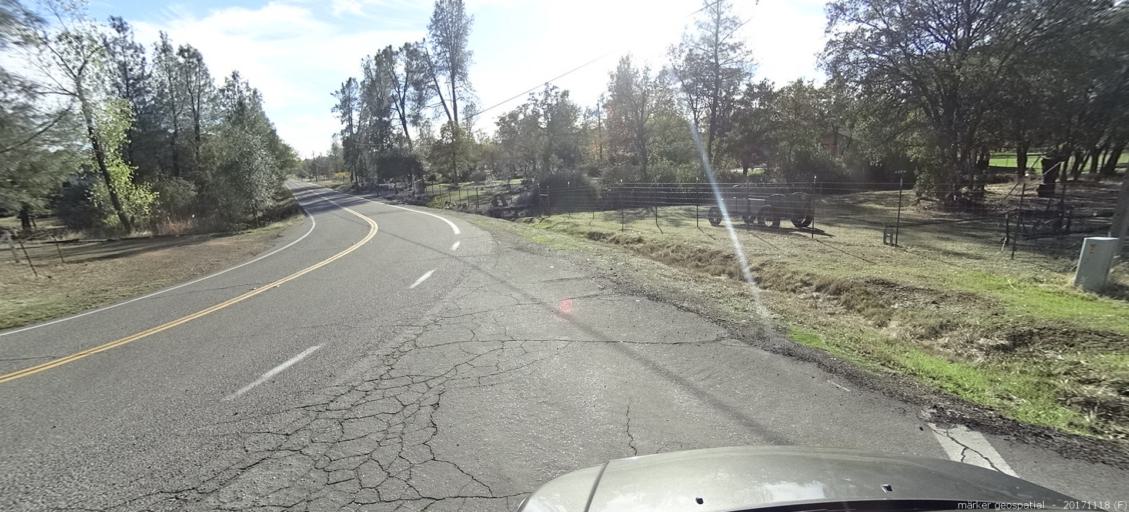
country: US
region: California
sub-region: Shasta County
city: Redding
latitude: 40.4849
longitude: -122.4549
